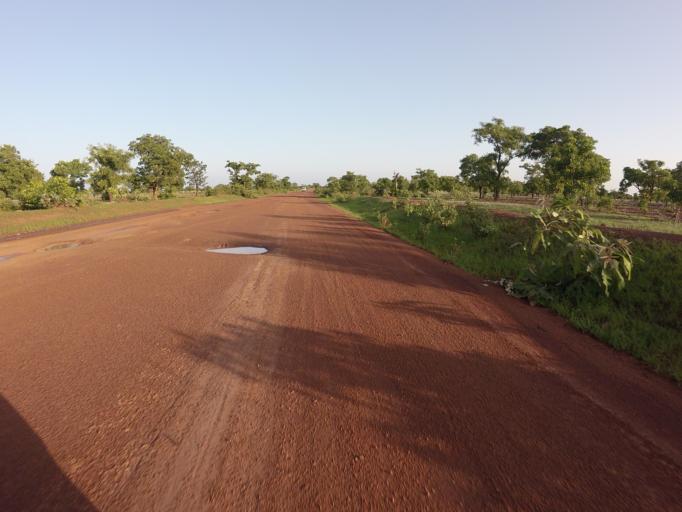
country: TG
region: Savanes
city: Sansanne-Mango
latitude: 10.2736
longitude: -0.0824
